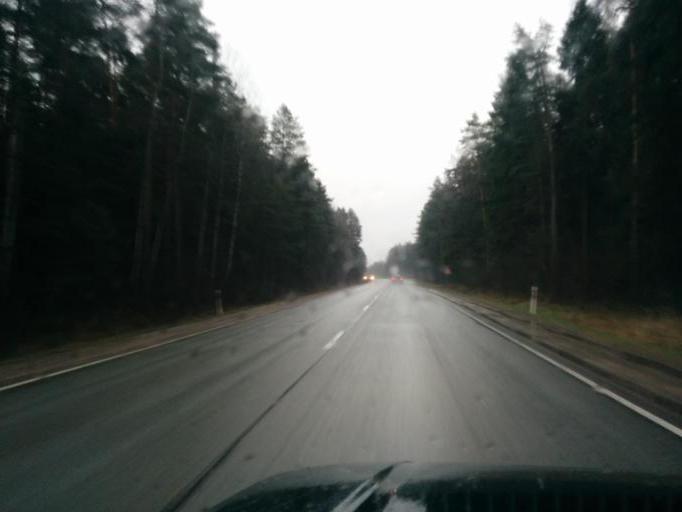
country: LV
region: Marupe
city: Marupe
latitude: 56.8294
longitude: 24.0513
